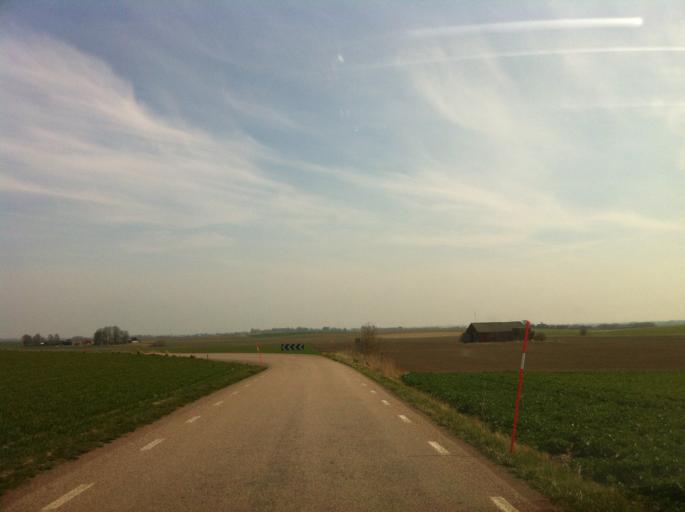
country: SE
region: Skane
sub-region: Svalovs Kommun
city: Svaloev
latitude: 55.9162
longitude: 13.0613
